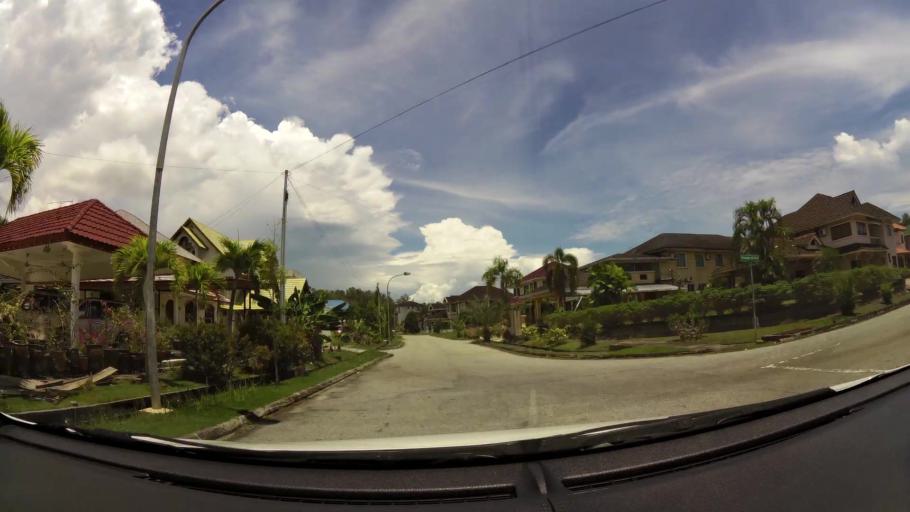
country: BN
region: Brunei and Muara
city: Bandar Seri Begawan
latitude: 4.9669
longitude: 114.9206
